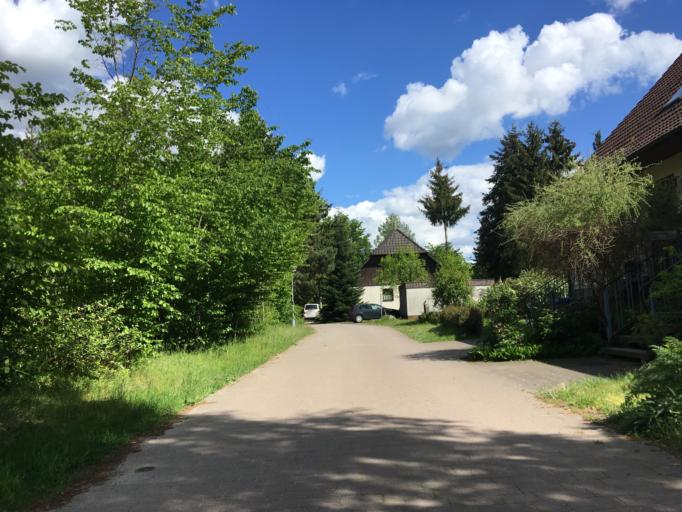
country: DE
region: Brandenburg
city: Rudnitz
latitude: 52.7274
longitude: 13.5947
